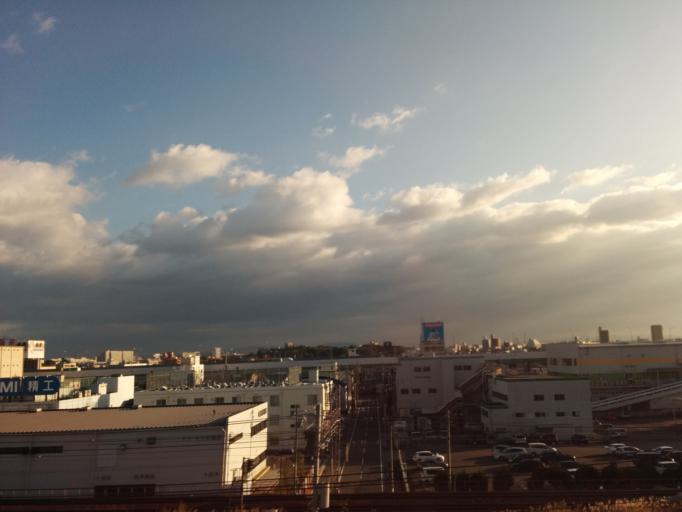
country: JP
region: Aichi
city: Nagoya-shi
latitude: 35.1015
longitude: 136.9224
